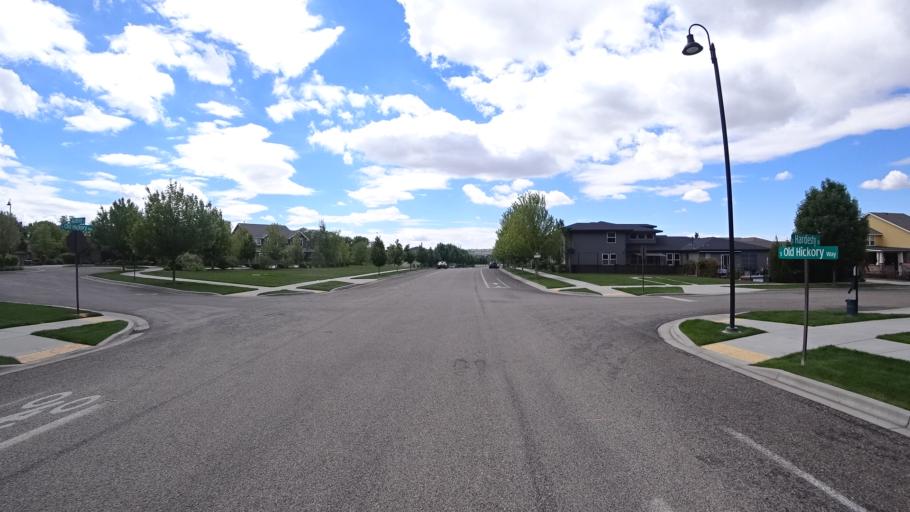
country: US
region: Idaho
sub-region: Ada County
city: Boise
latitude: 43.5798
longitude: -116.1317
